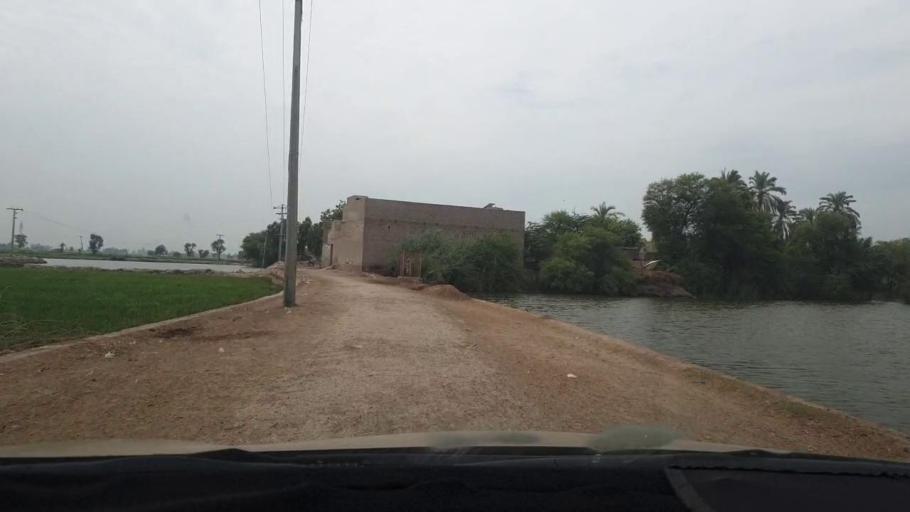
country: PK
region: Sindh
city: Naudero
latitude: 27.6778
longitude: 68.3347
